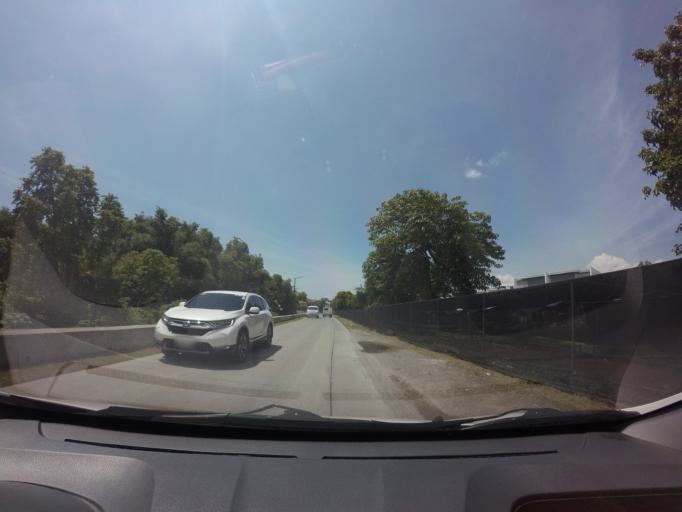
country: PH
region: Calabarzon
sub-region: Province of Rizal
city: Las Pinas
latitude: 14.4250
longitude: 120.9870
